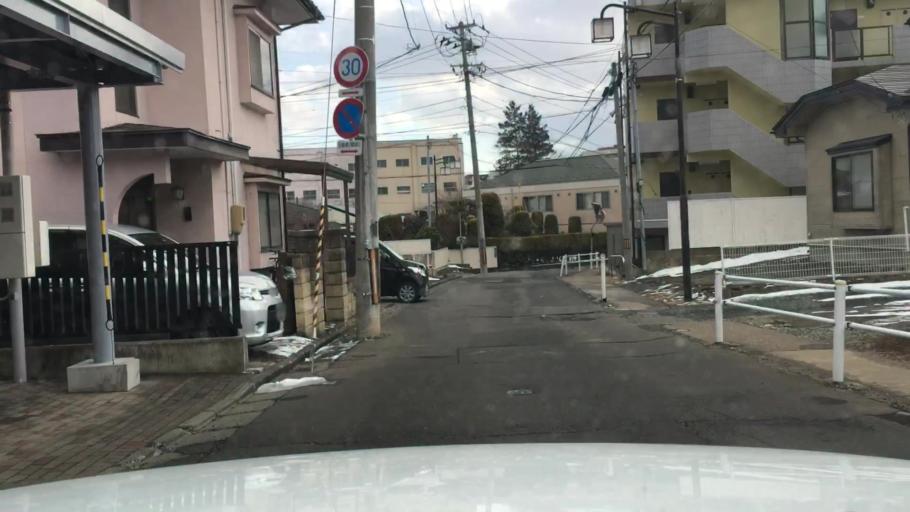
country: JP
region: Iwate
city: Morioka-shi
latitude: 39.7108
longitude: 141.1440
